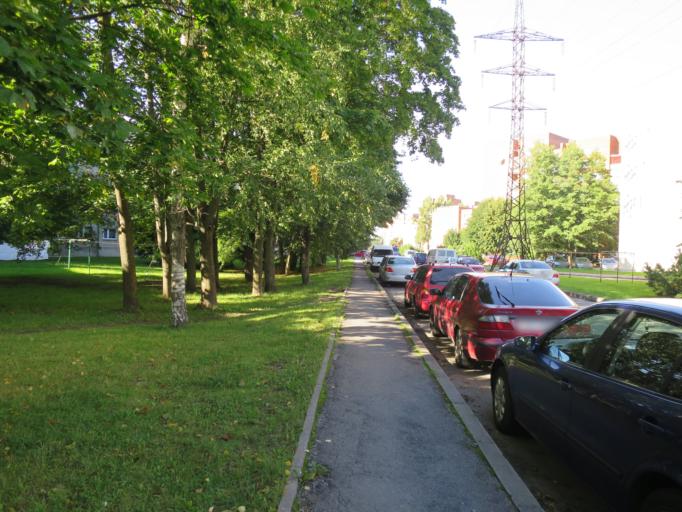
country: EE
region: Harju
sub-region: Tallinna linn
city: Tallinn
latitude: 59.4053
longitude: 24.7079
